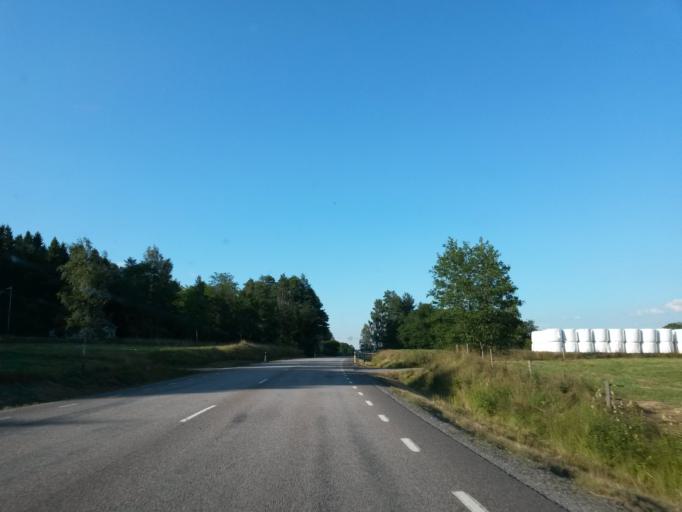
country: SE
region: Vaestra Goetaland
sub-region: Alingsas Kommun
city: Alingsas
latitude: 57.9959
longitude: 12.6084
